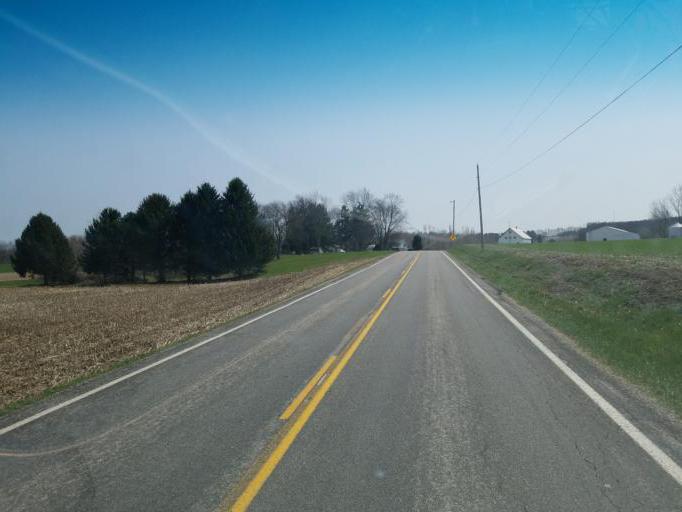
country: US
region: Ohio
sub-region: Richland County
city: Lexington
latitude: 40.6214
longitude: -82.5902
